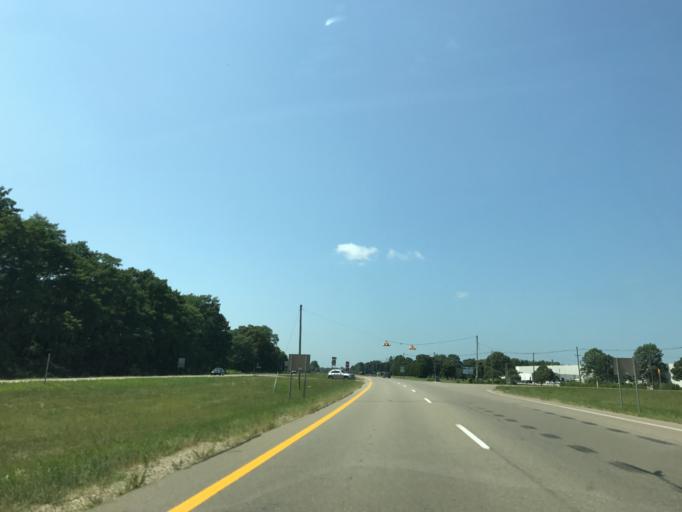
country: US
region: Michigan
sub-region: Berrien County
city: Niles
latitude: 41.8052
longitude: -86.2965
